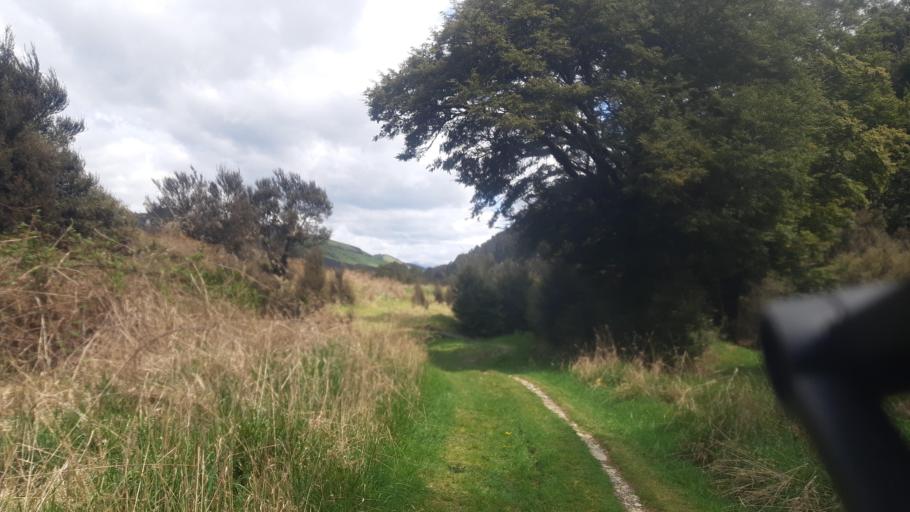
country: NZ
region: Tasman
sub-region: Tasman District
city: Wakefield
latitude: -41.7935
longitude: 172.8371
